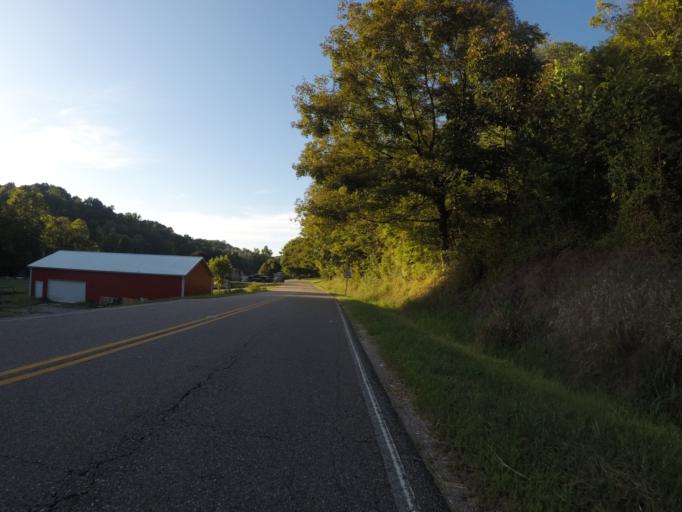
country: US
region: Ohio
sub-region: Lawrence County
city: Coal Grove
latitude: 38.5636
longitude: -82.5500
